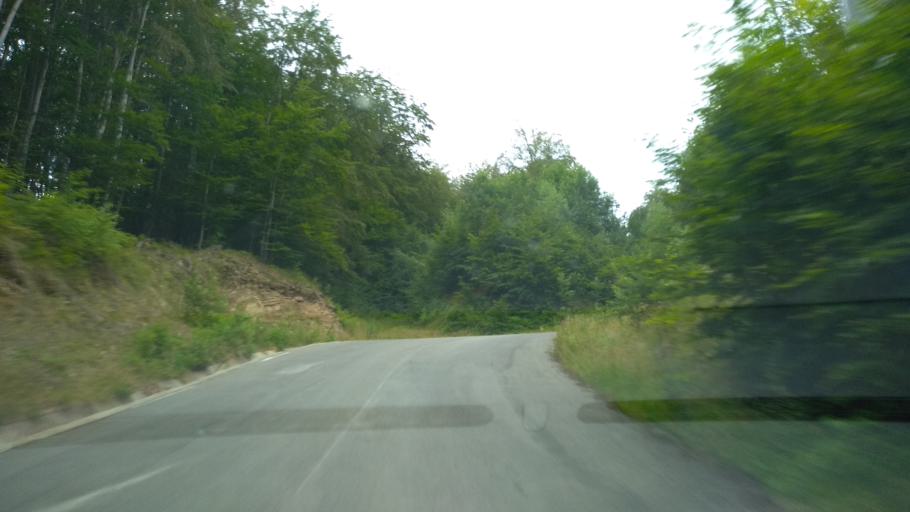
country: RO
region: Hunedoara
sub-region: Municipiul  Vulcan
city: Jiu-Paroseni
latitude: 45.3384
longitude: 23.2912
